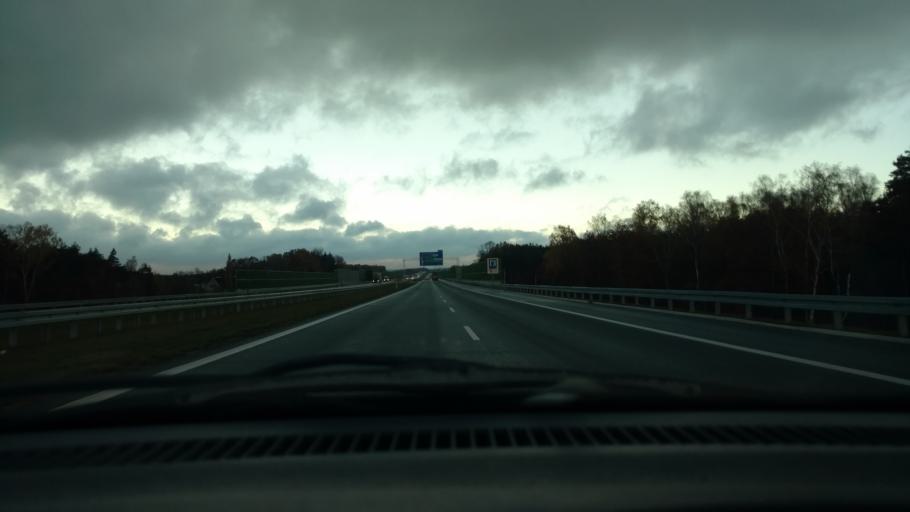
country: PL
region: Lodz Voivodeship
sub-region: Powiat lodzki wschodni
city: Andrespol
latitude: 51.7349
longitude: 19.6027
